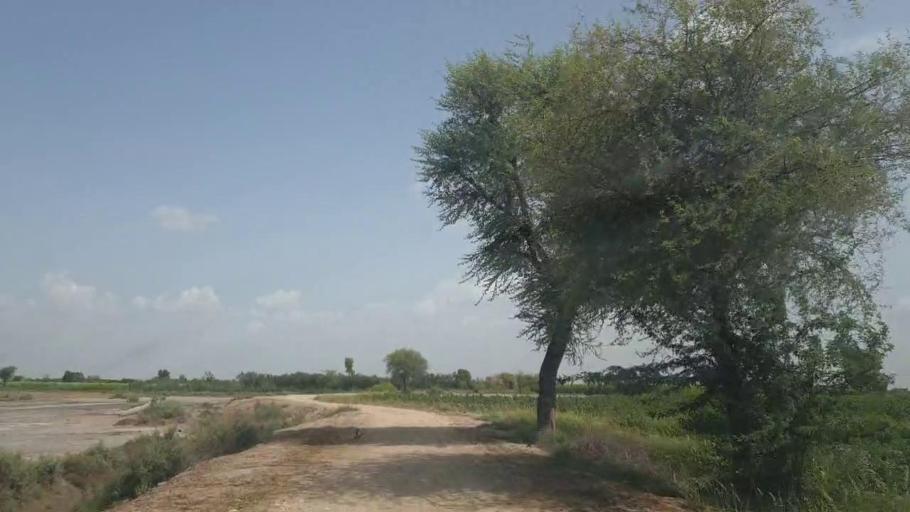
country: PK
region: Sindh
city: Tando Bago
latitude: 24.7500
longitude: 69.1777
